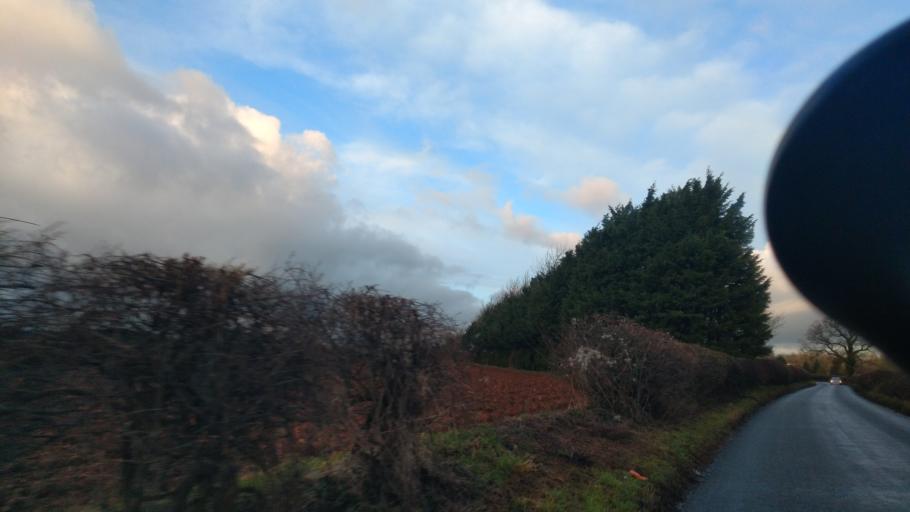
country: GB
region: England
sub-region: Wiltshire
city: Biddestone
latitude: 51.4520
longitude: -2.1883
